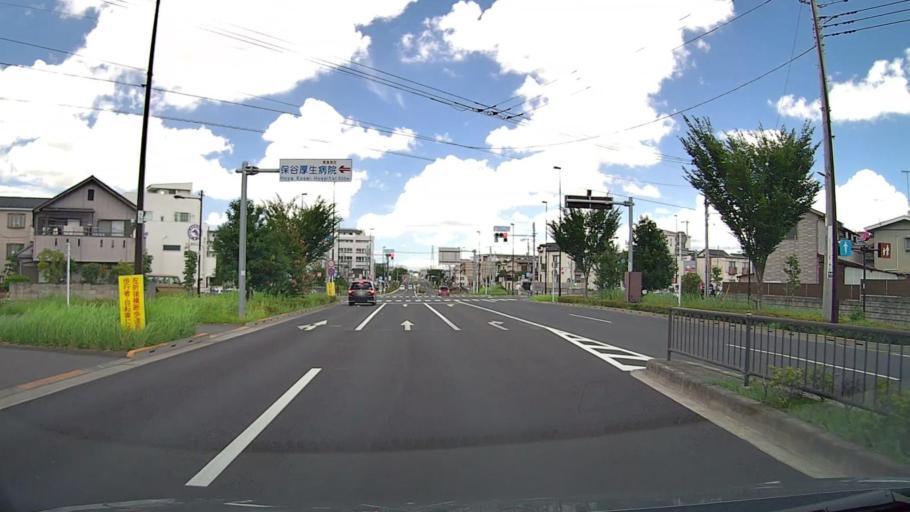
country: JP
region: Tokyo
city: Tanashicho
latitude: 35.7505
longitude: 139.5591
